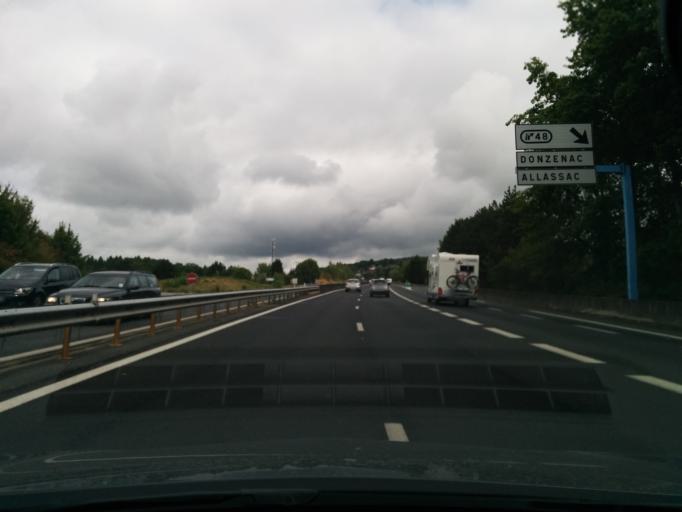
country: FR
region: Limousin
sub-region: Departement de la Correze
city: Donzenac
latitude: 45.2257
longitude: 1.5112
